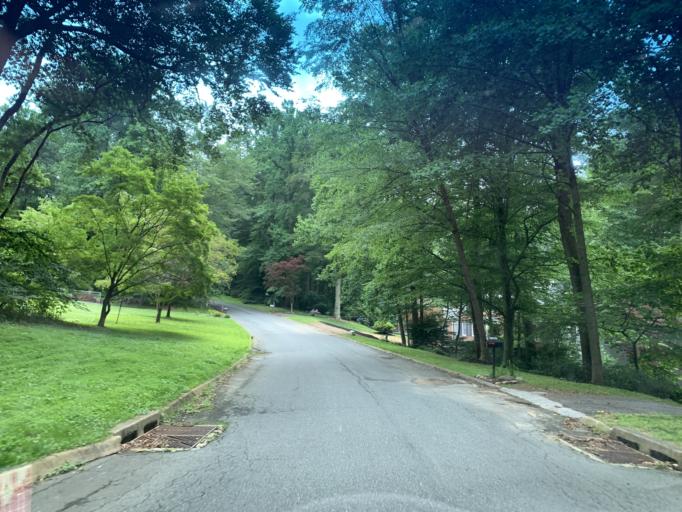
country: US
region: Maryland
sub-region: Harford County
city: Fallston
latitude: 39.5431
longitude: -76.4334
